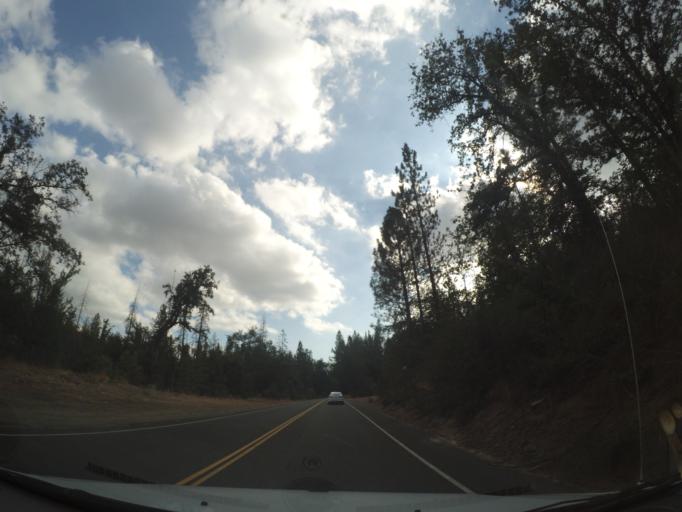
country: US
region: California
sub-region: Mariposa County
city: Midpines
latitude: 37.5279
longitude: -119.9183
